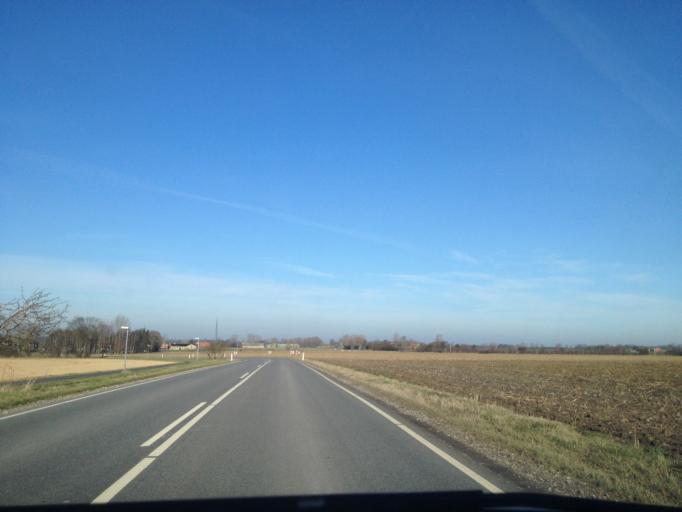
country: DK
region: South Denmark
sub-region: Nyborg Kommune
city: Ullerslev
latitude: 55.3743
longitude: 10.7275
